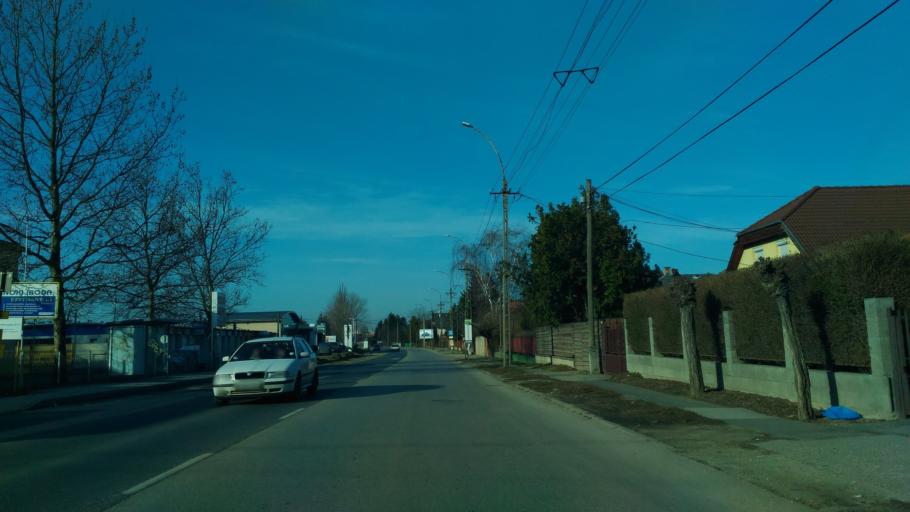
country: HU
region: Pest
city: Erd
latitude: 47.3712
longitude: 18.8912
